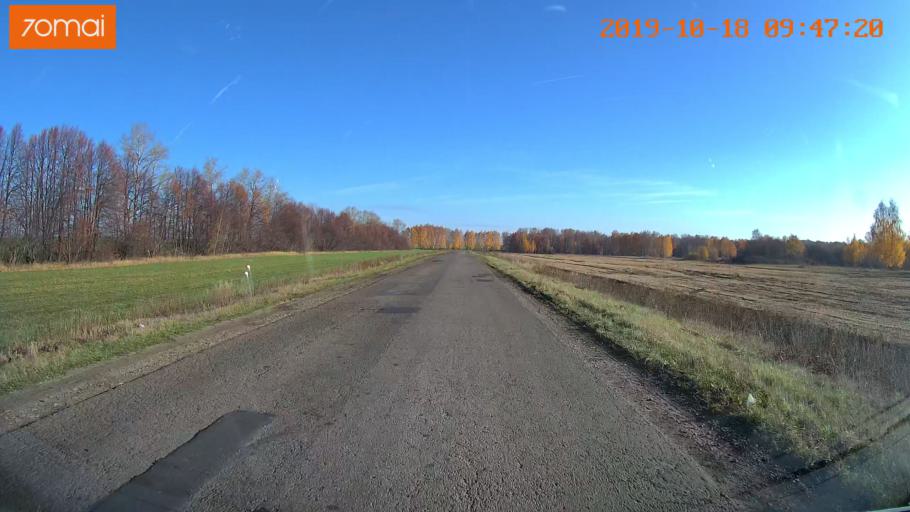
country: RU
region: Tula
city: Kazachka
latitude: 53.3178
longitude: 38.2295
